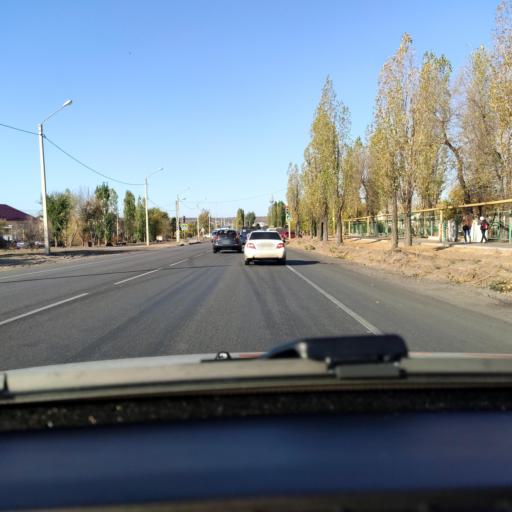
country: RU
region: Voronezj
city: Pridonskoy
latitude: 51.7050
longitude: 39.0757
